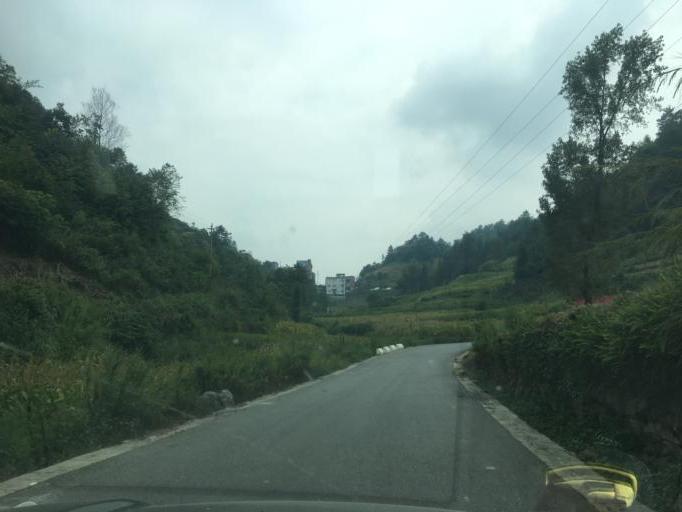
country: CN
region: Guangxi Zhuangzu Zizhiqu
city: Tongle
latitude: 25.3247
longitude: 106.0351
